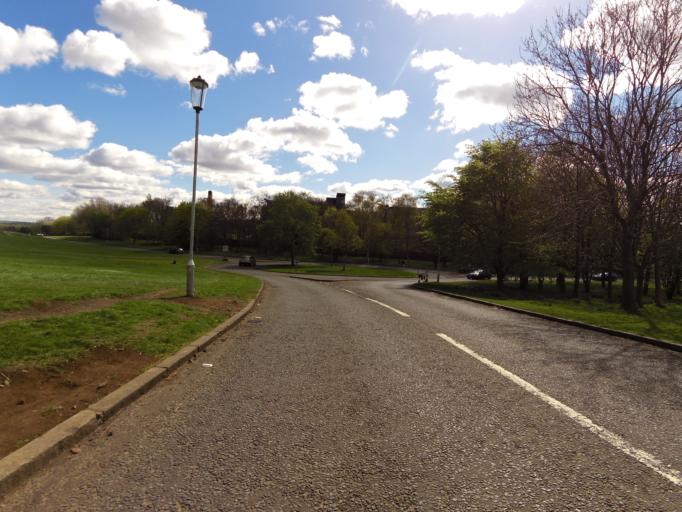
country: GB
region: Scotland
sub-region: Edinburgh
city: Edinburgh
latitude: 55.9422
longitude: -3.1704
